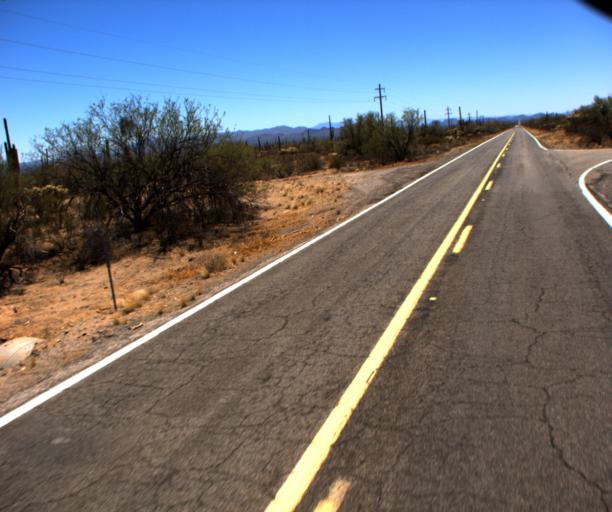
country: US
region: Arizona
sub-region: Pima County
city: Sells
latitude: 32.1345
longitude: -112.0931
